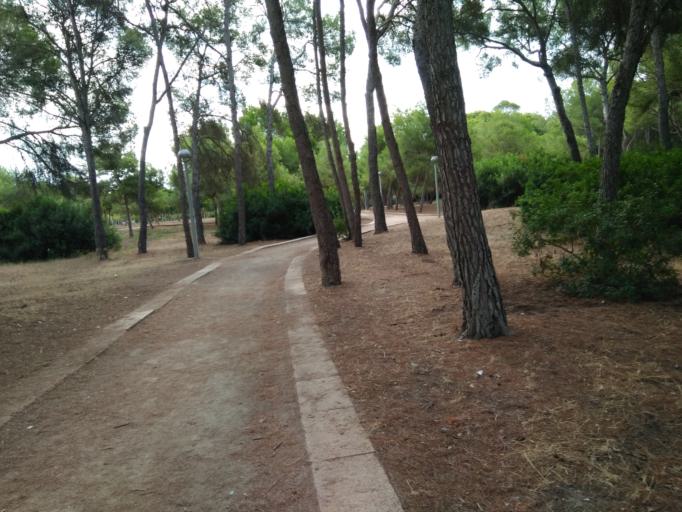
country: ES
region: Balearic Islands
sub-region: Illes Balears
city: s'Arenal
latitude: 39.5284
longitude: 2.7383
